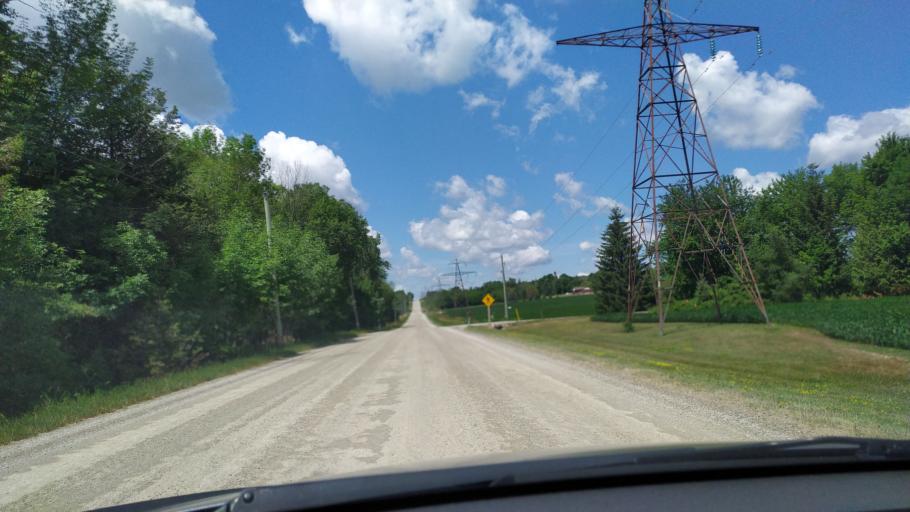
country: CA
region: Ontario
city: Stratford
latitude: 43.3876
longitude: -80.7937
